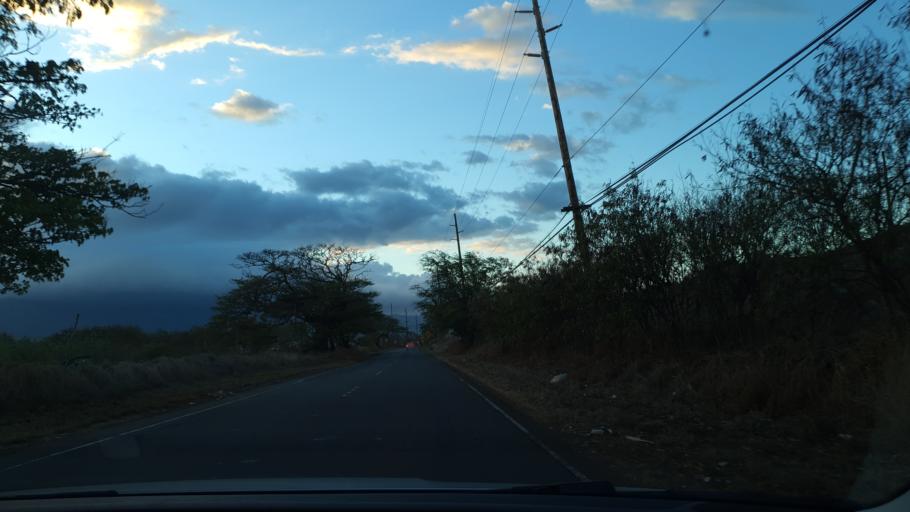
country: US
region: Hawaii
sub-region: Maui County
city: Kahului
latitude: 20.8710
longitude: -156.4377
